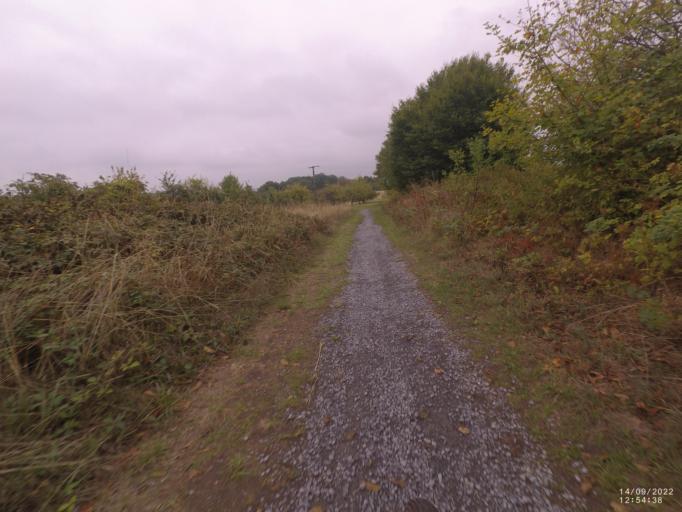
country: DE
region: Bavaria
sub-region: Regierungsbezirk Unterfranken
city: Glattbach
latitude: 50.0086
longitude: 9.1376
